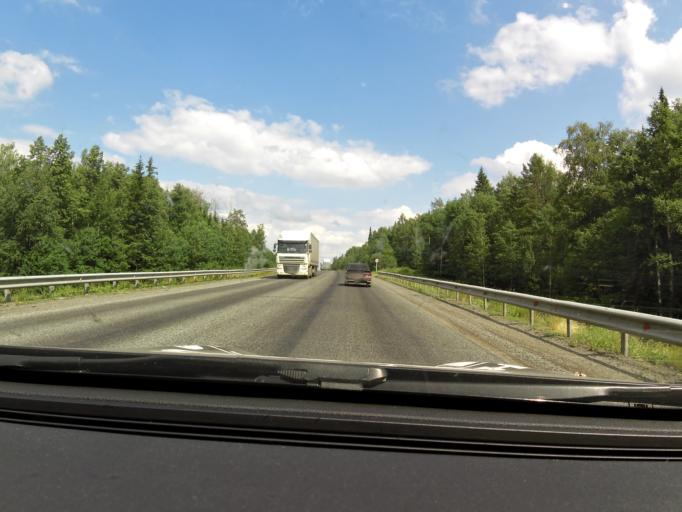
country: RU
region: Sverdlovsk
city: Arti
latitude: 56.7858
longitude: 58.5342
